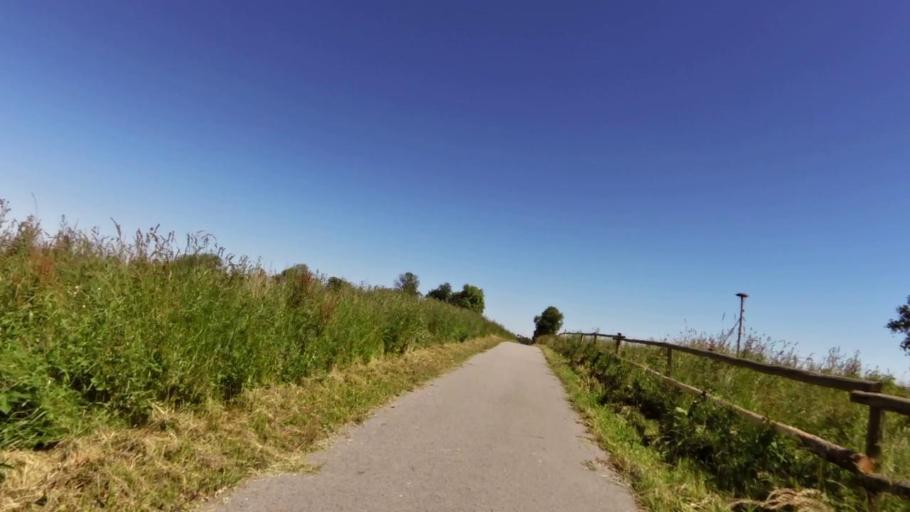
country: PL
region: West Pomeranian Voivodeship
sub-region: Powiat kolobrzeski
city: Dygowo
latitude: 54.0477
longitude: 15.7608
